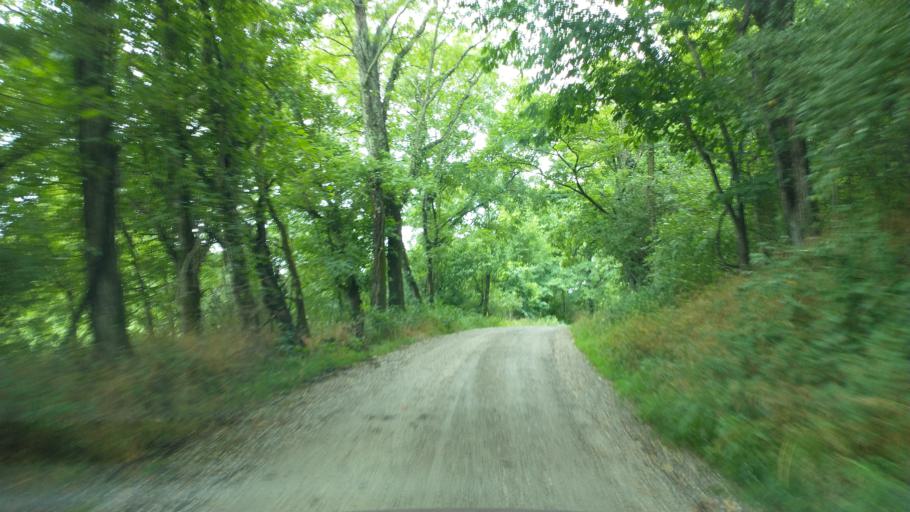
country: US
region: Ohio
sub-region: Meigs County
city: Middleport
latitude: 38.9278
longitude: -82.0612
